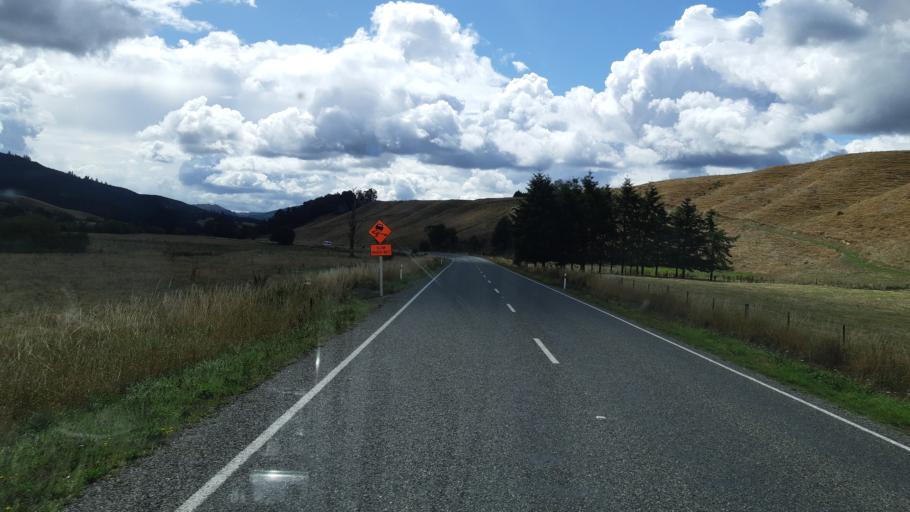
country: NZ
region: Tasman
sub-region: Tasman District
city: Wakefield
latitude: -41.5732
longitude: 172.7734
